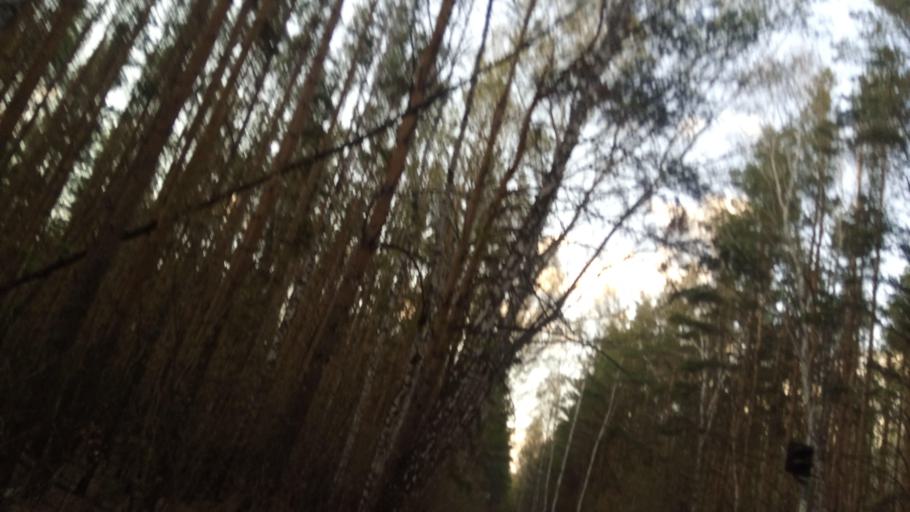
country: RU
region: Chelyabinsk
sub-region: Gorod Chelyabinsk
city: Chelyabinsk
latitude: 55.1634
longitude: 61.3172
